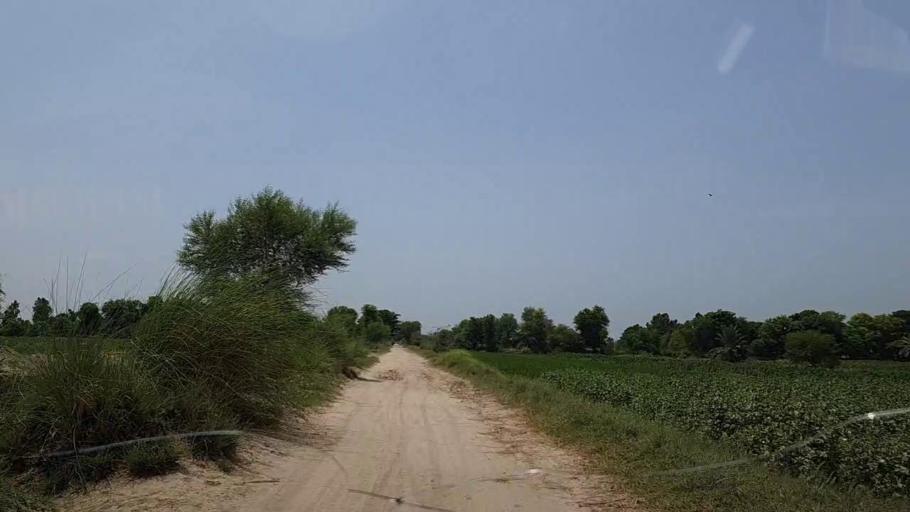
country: PK
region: Sindh
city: Khanpur
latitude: 27.7963
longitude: 69.4679
